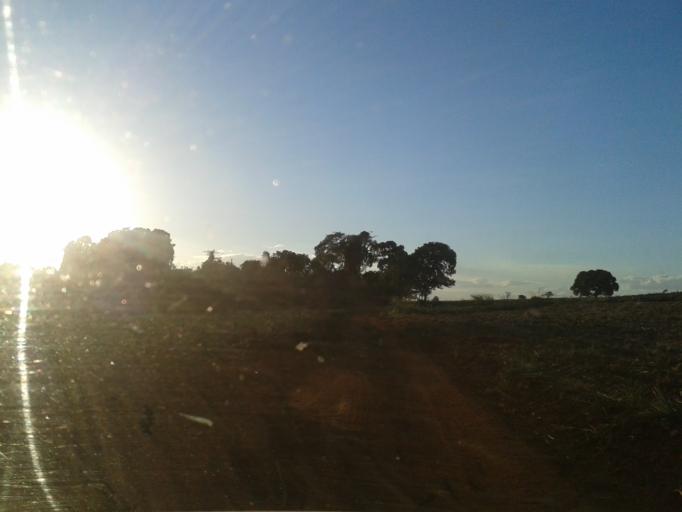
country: BR
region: Minas Gerais
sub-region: Centralina
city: Centralina
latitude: -18.6010
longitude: -49.3071
